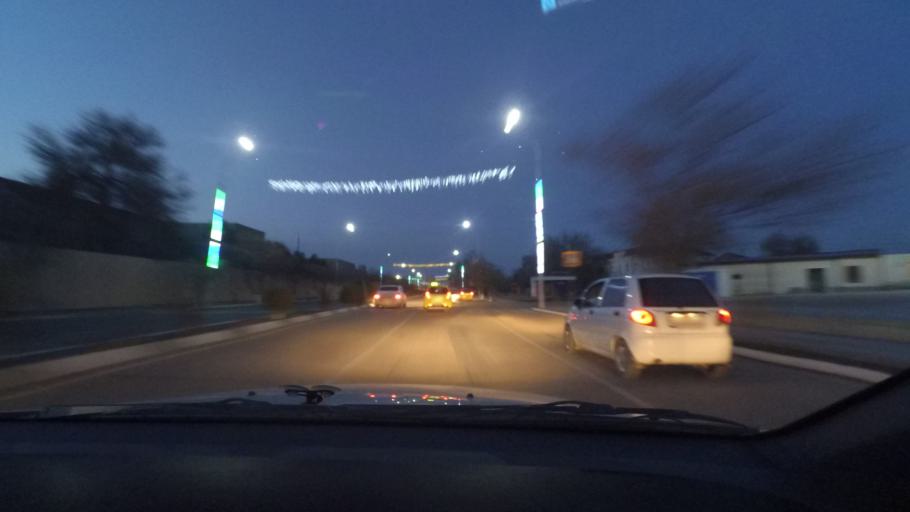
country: UZ
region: Bukhara
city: Bukhara
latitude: 39.7789
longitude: 64.4096
